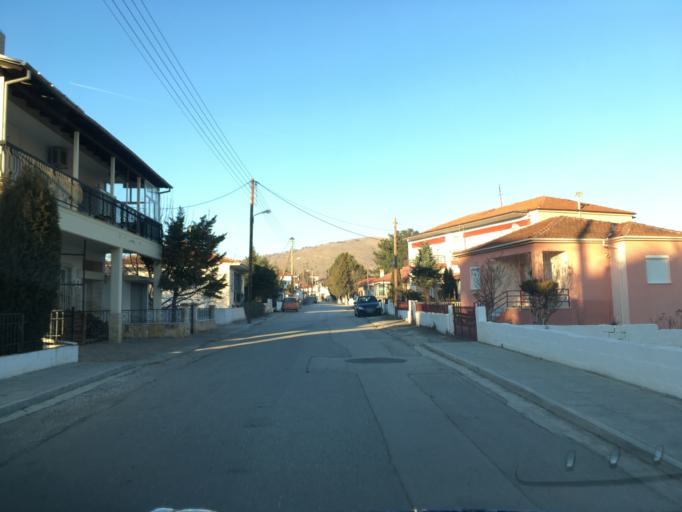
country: GR
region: West Macedonia
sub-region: Nomos Kozanis
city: Kozani
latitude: 40.2898
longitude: 21.7348
